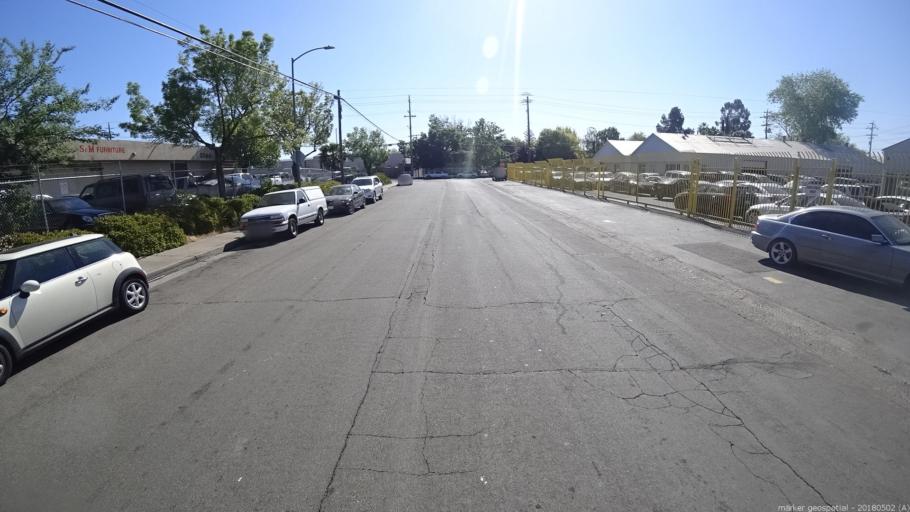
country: US
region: California
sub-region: Sacramento County
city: Arden-Arcade
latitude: 38.6098
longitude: -121.4242
